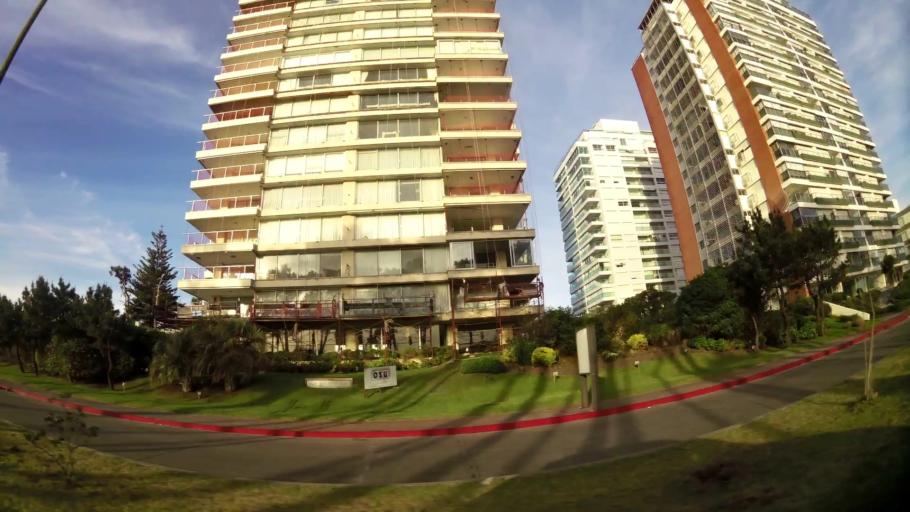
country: UY
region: Maldonado
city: Punta del Este
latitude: -34.9434
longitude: -54.9443
